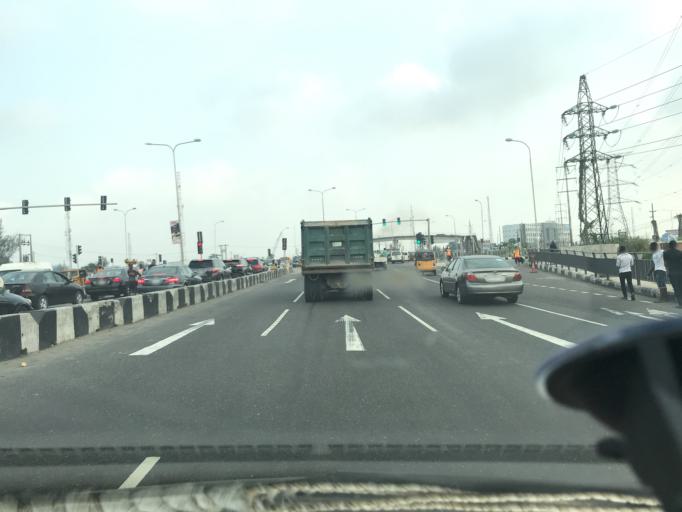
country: NG
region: Lagos
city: Ikoyi
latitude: 6.4599
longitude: 3.5554
